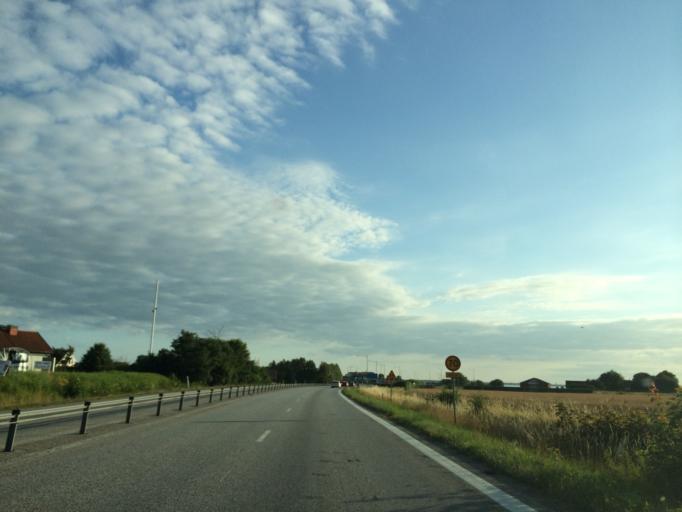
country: SE
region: Skane
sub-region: Vellinge Kommun
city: Hollviken
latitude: 55.4277
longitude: 12.9652
